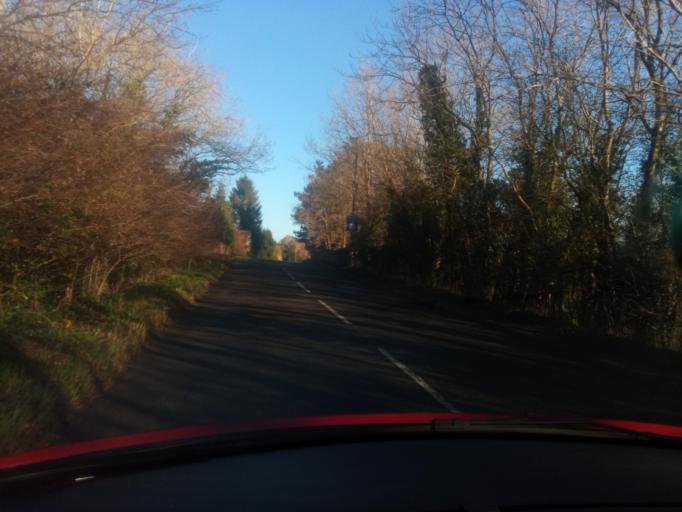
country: GB
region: England
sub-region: Derbyshire
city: Belper
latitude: 53.0178
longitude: -1.5476
